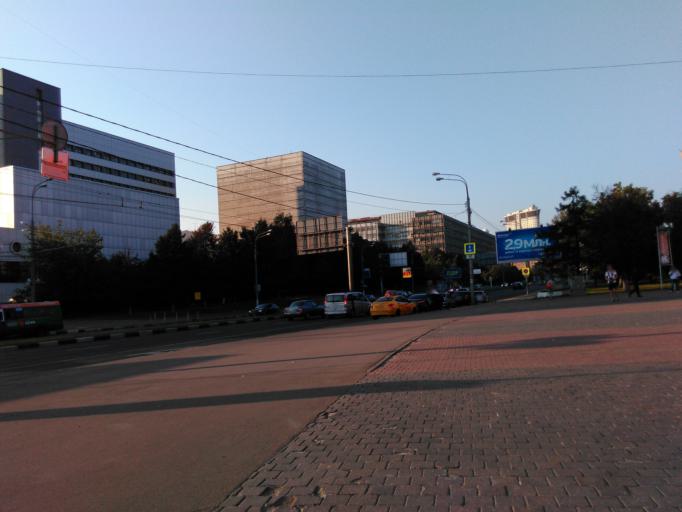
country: RU
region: Moskovskaya
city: Cheremushki
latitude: 55.6562
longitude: 37.5400
